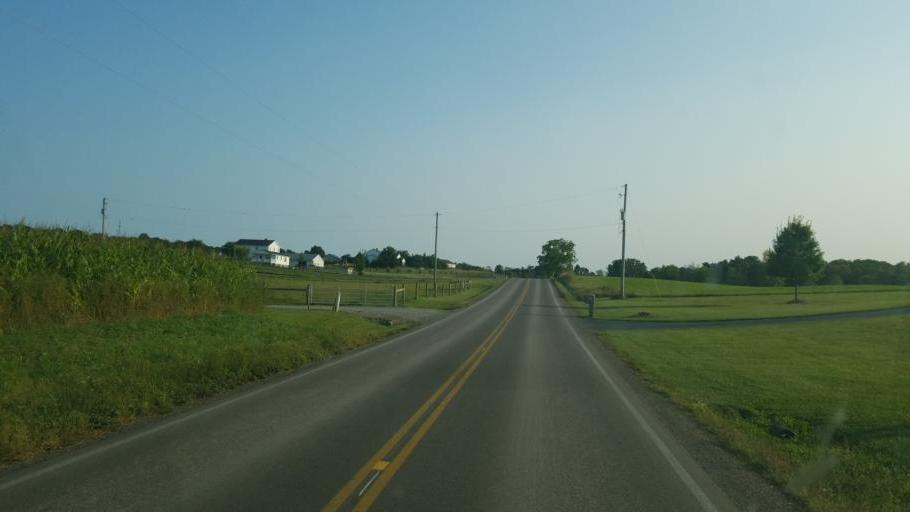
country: US
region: Ohio
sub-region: Wayne County
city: Apple Creek
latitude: 40.7323
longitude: -81.8193
